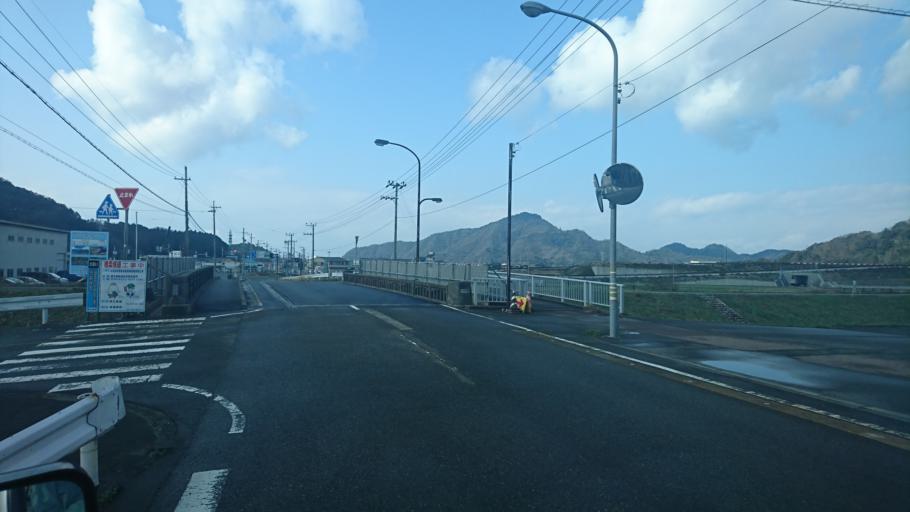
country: JP
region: Tottori
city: Tottori
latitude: 35.6092
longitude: 134.4717
